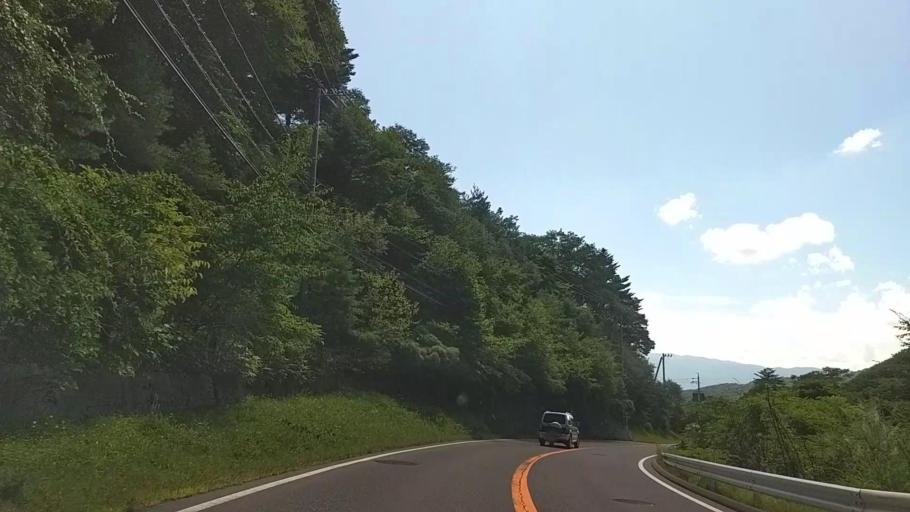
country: JP
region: Nagano
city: Chino
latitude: 36.0881
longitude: 138.2234
